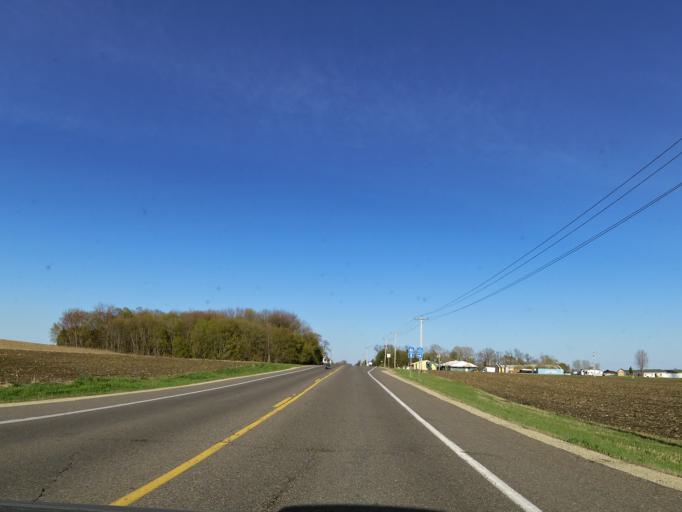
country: US
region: Minnesota
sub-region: Rice County
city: Northfield
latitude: 44.5438
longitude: -93.2036
